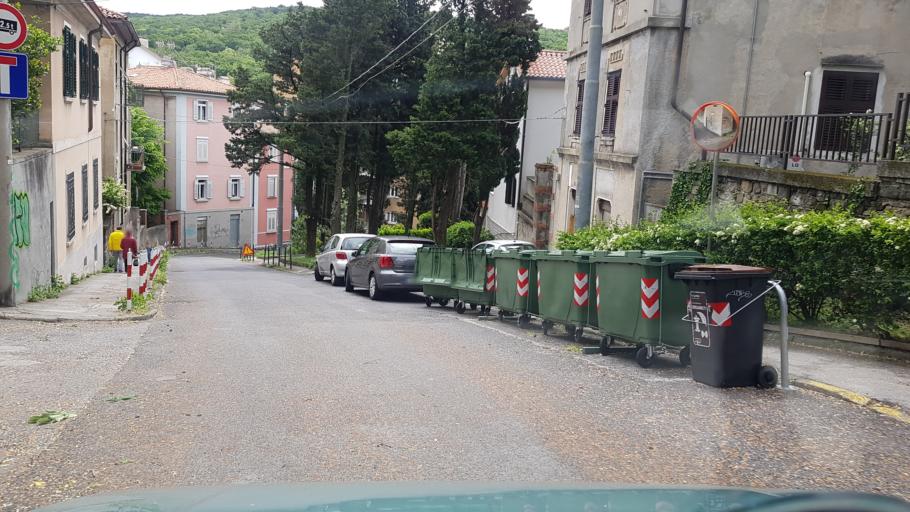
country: IT
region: Friuli Venezia Giulia
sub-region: Provincia di Trieste
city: Trieste
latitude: 45.6567
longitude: 13.7944
